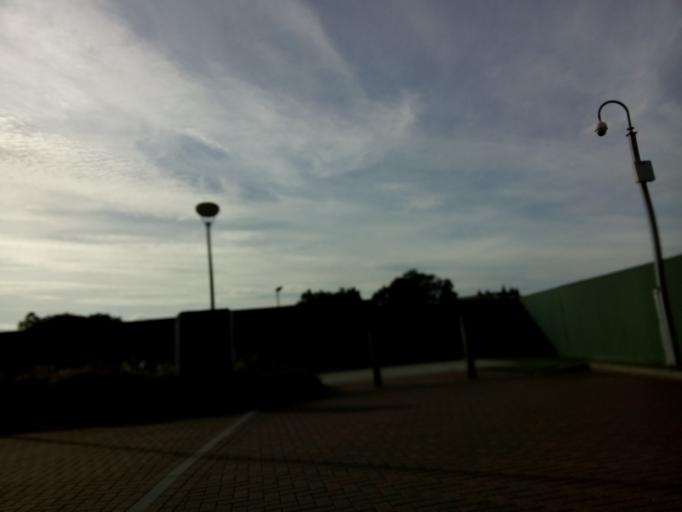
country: GB
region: England
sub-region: Norfolk
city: Norwich
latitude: 52.6355
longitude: 1.3048
